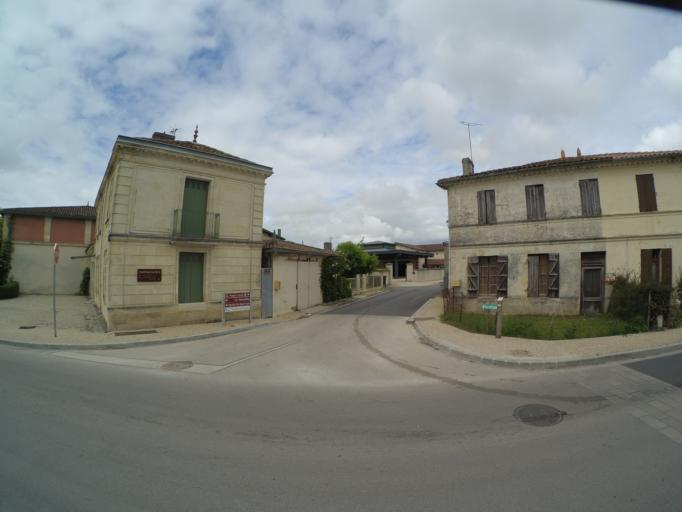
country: FR
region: Aquitaine
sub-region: Departement de la Gironde
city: Margaux
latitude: 45.0359
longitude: -0.6688
